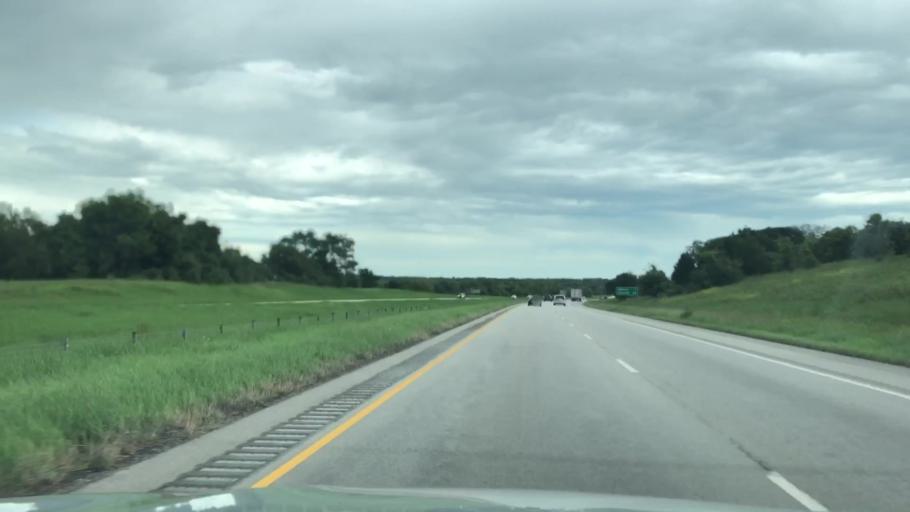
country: US
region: Texas
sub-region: Fayette County
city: Schulenburg
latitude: 29.6955
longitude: -96.8885
